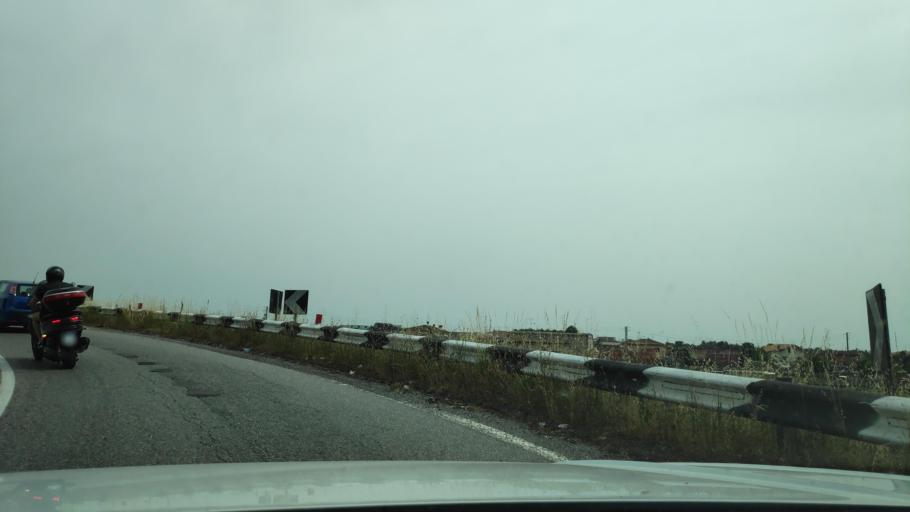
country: IT
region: Lombardy
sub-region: Provincia di Brescia
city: Orzinuovi
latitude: 45.4137
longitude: 9.9263
